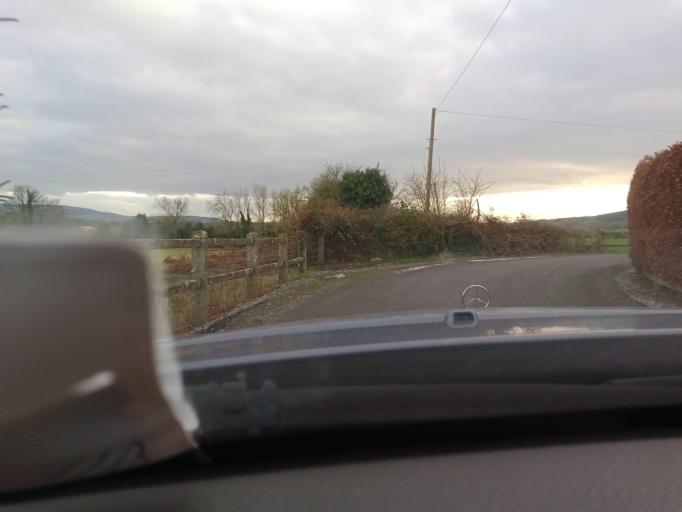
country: IE
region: Leinster
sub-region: Kilkenny
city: Graiguenamanagh
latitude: 52.5219
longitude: -6.9441
